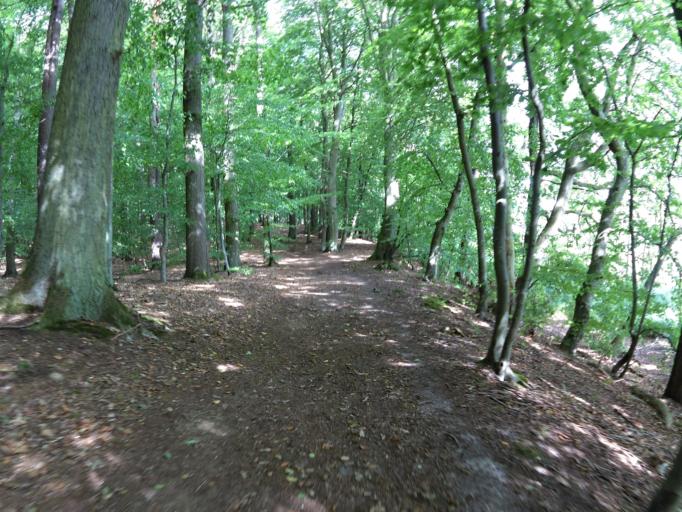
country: DE
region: Mecklenburg-Vorpommern
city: Seebad Bansin
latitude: 53.9543
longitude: 14.1087
